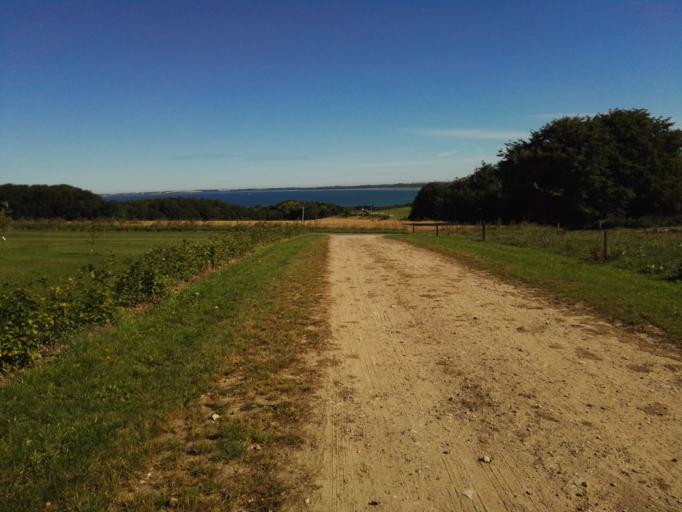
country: DK
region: Zealand
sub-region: Odsherred Kommune
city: Asnaes
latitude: 55.8388
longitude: 11.4799
